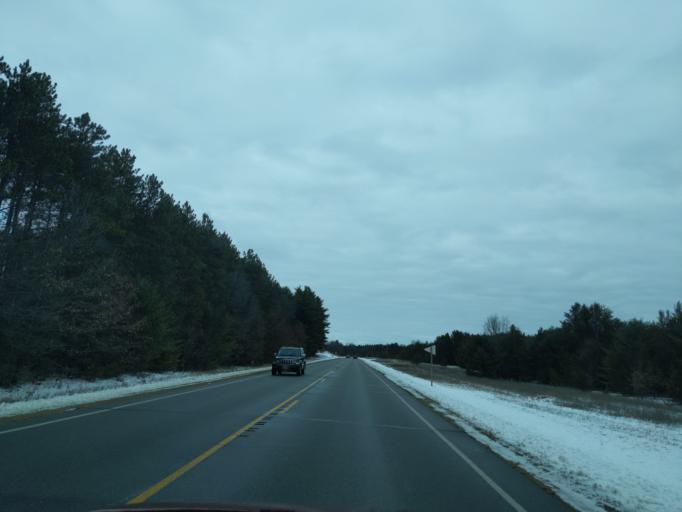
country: US
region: Wisconsin
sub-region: Waushara County
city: Wautoma
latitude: 43.9494
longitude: -89.3176
